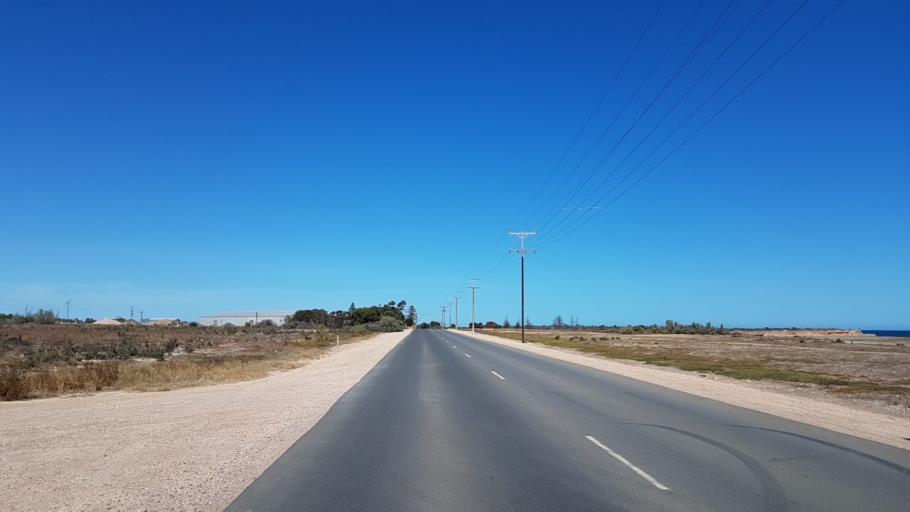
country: AU
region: South Australia
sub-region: Copper Coast
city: Wallaroo
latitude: -33.9333
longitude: 137.6111
